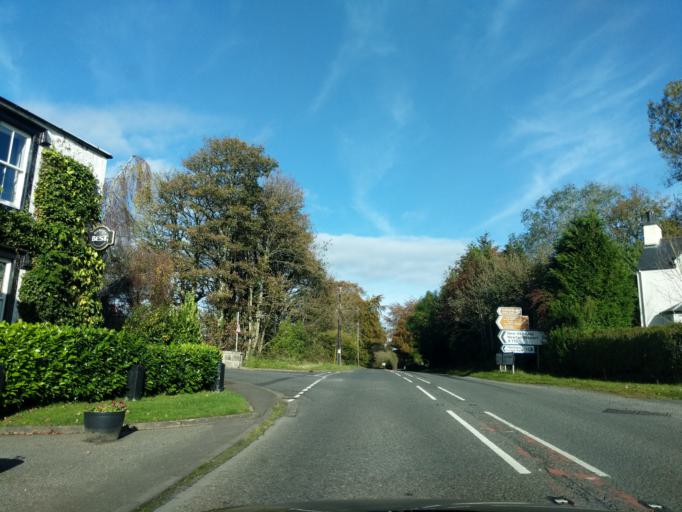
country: GB
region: Scotland
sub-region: Dumfries and Galloway
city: Castle Douglas
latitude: 55.0807
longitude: -4.1301
